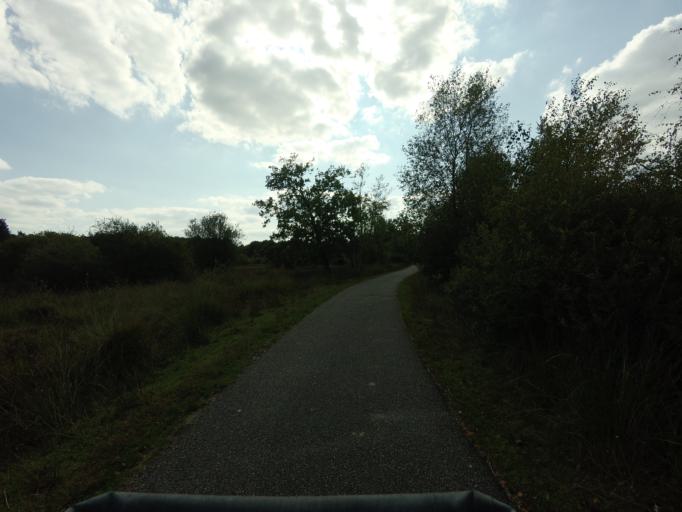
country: NL
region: Drenthe
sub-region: Gemeente Hoogeveen
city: Hoogeveen
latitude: 52.7974
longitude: 6.4436
